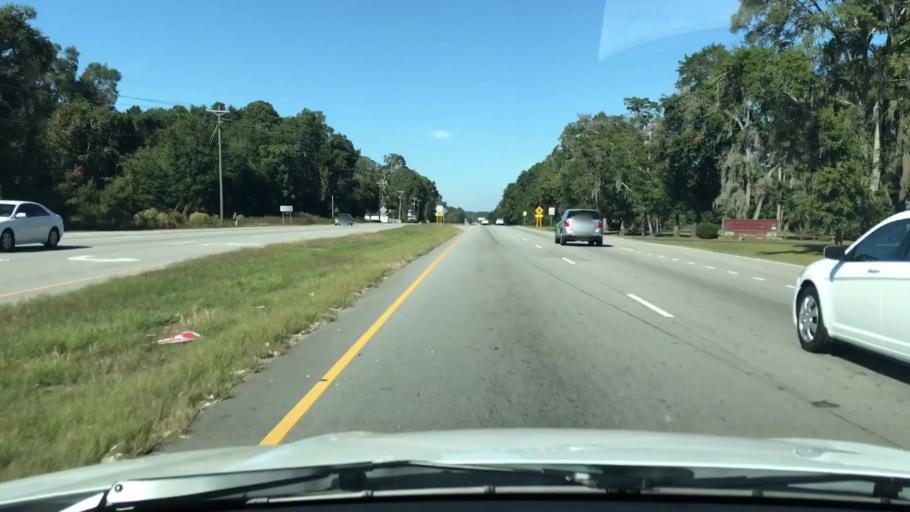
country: US
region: South Carolina
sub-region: Beaufort County
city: Burton
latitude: 32.4936
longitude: -80.7420
